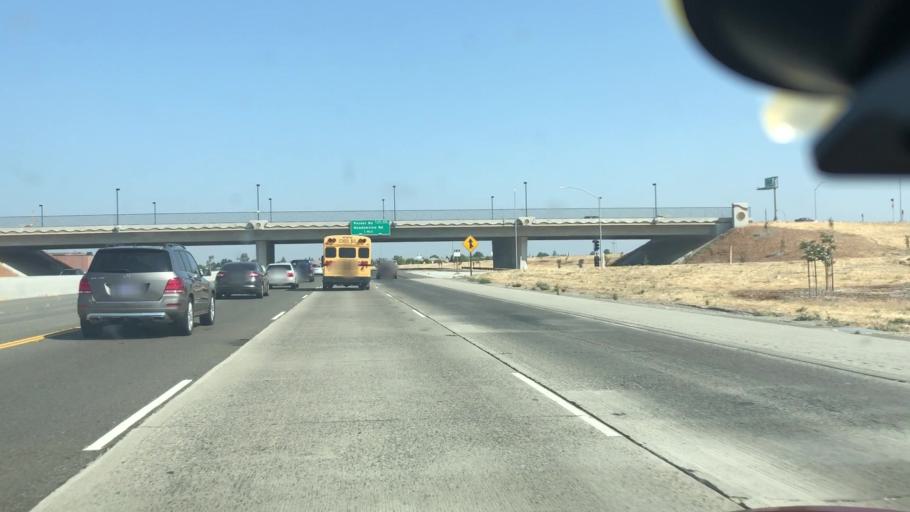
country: US
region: California
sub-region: Sacramento County
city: Parkway
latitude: 38.4652
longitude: -121.4964
